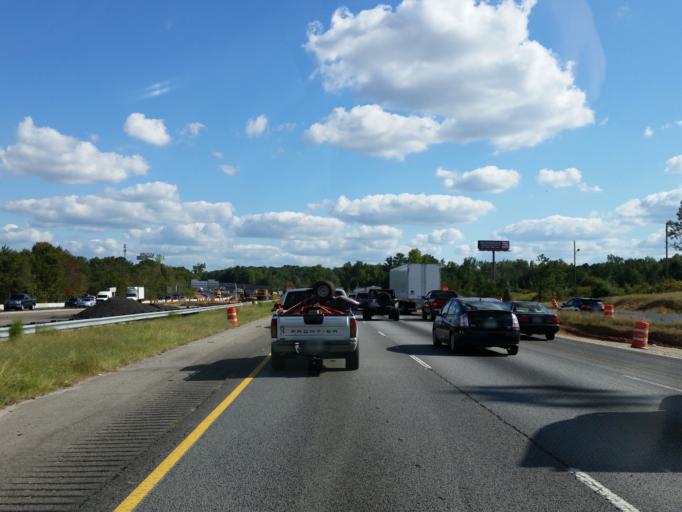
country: US
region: Georgia
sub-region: Henry County
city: McDonough
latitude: 33.4601
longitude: -84.2092
